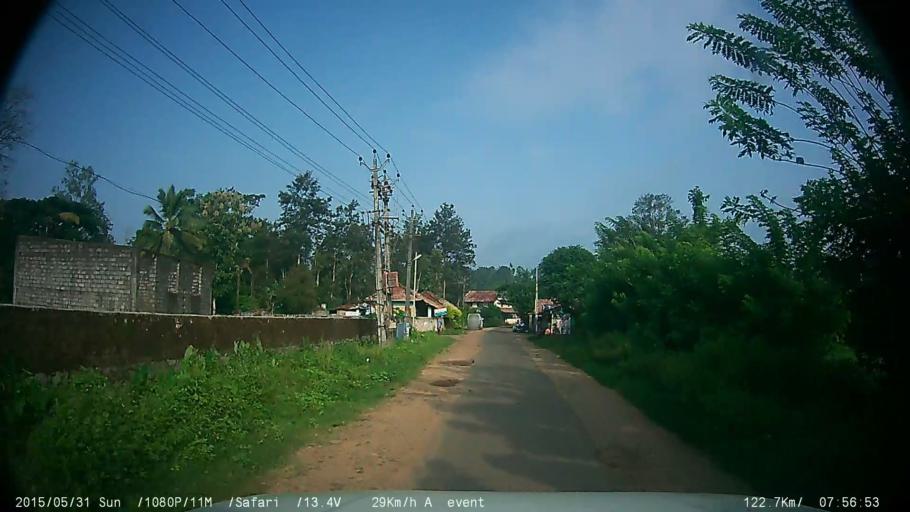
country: IN
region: Kerala
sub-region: Wayanad
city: Kalpetta
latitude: 11.6309
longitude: 76.0672
